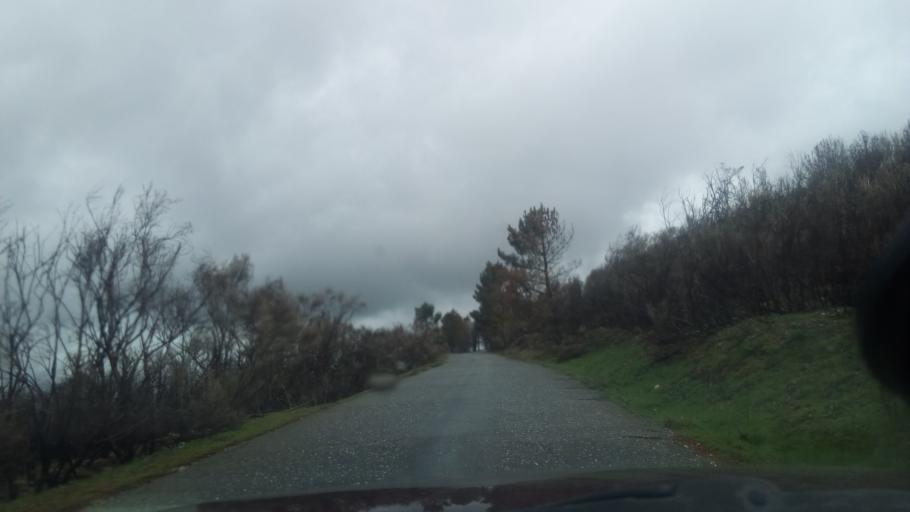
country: PT
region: Guarda
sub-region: Celorico da Beira
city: Celorico da Beira
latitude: 40.5396
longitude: -7.4513
